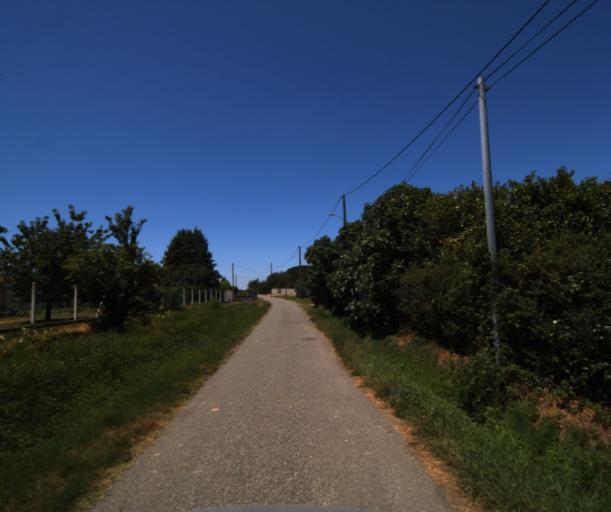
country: FR
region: Midi-Pyrenees
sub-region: Departement de la Haute-Garonne
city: Seysses
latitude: 43.4671
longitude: 1.3009
